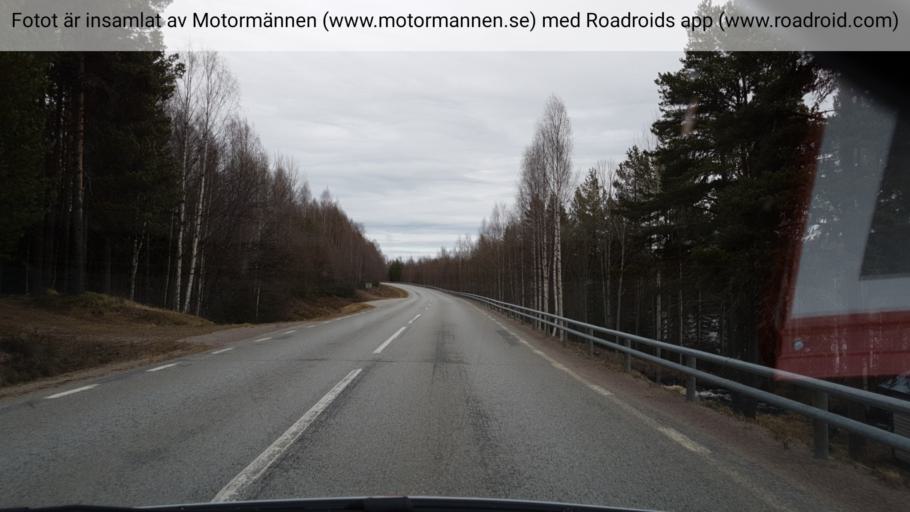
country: SE
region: Vaesterbotten
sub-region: Asele Kommun
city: Asele
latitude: 63.7934
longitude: 17.0904
